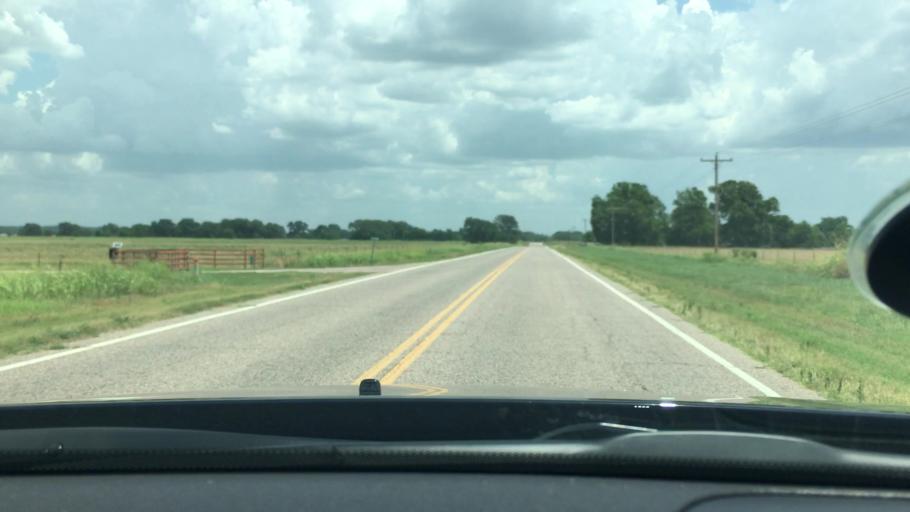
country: US
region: Texas
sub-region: Grayson County
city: Sherwood Shores
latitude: 33.9840
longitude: -96.9310
